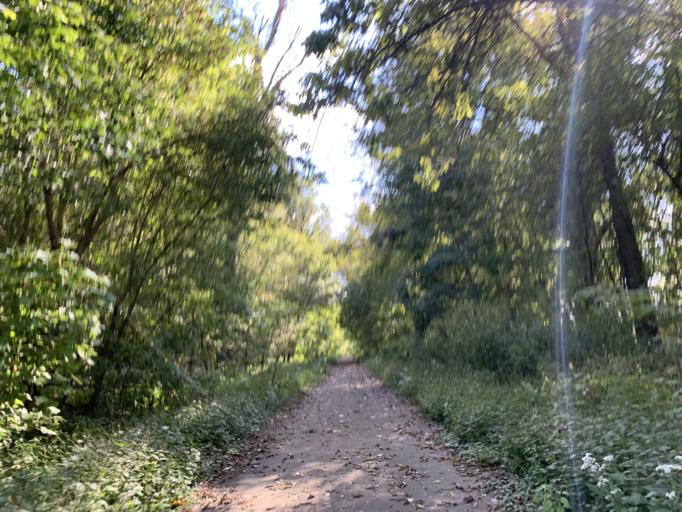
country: US
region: Indiana
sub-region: Floyd County
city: New Albany
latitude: 38.2606
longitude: -85.8316
